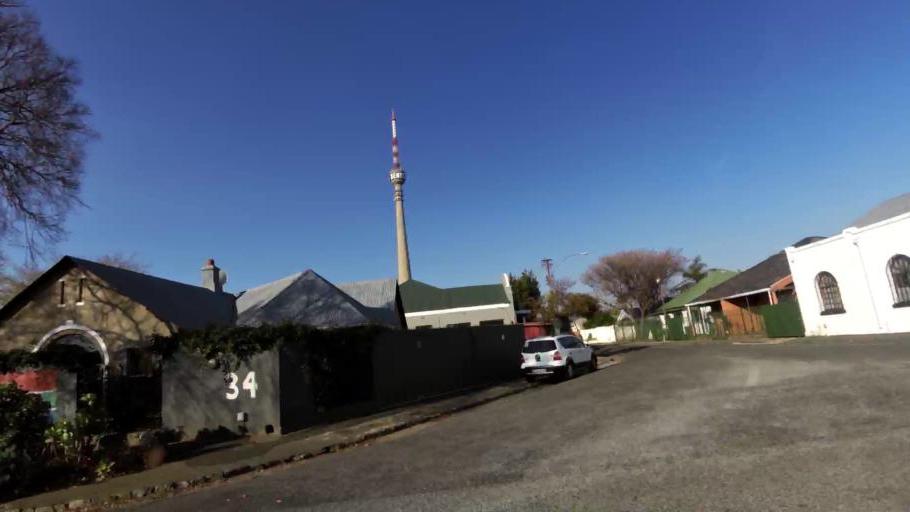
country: ZA
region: Gauteng
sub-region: City of Johannesburg Metropolitan Municipality
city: Johannesburg
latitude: -26.1926
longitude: 28.0027
